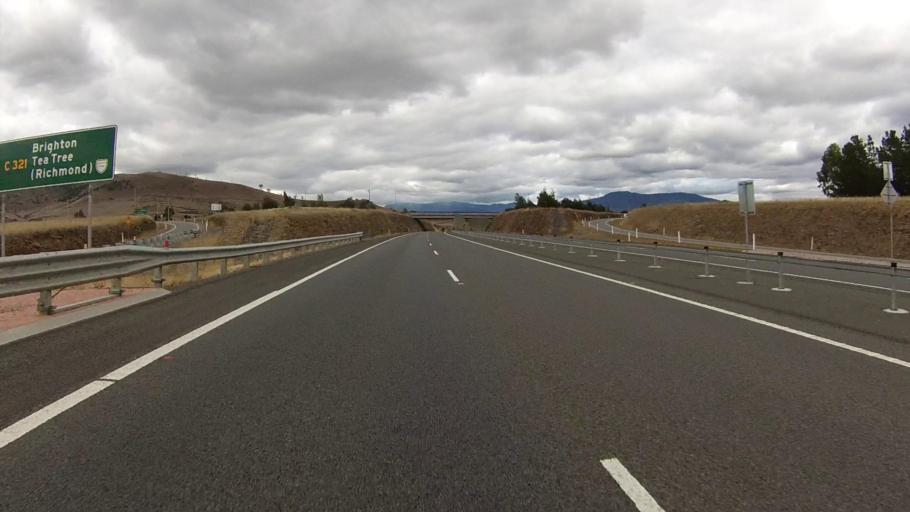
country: AU
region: Tasmania
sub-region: Brighton
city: Bridgewater
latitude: -42.6937
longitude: 147.2781
